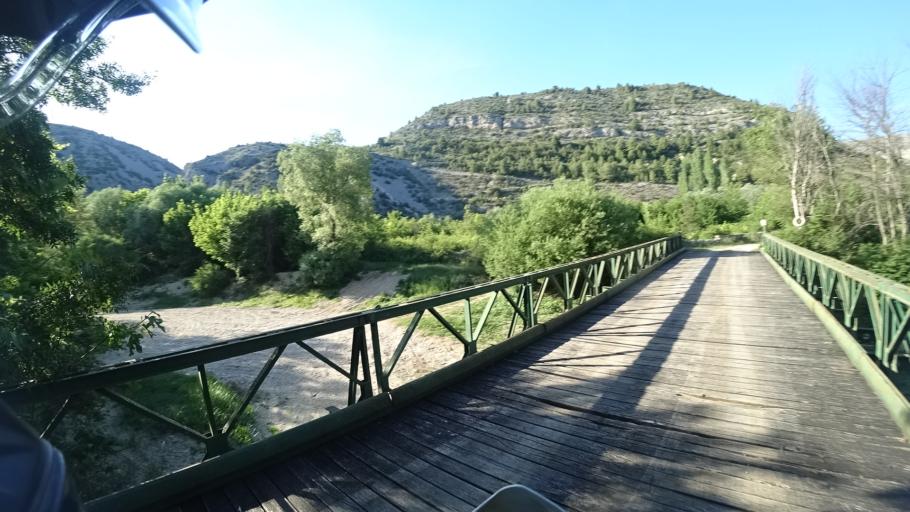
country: HR
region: Sibensko-Kniniska
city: Drnis
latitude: 43.8264
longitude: 16.0221
